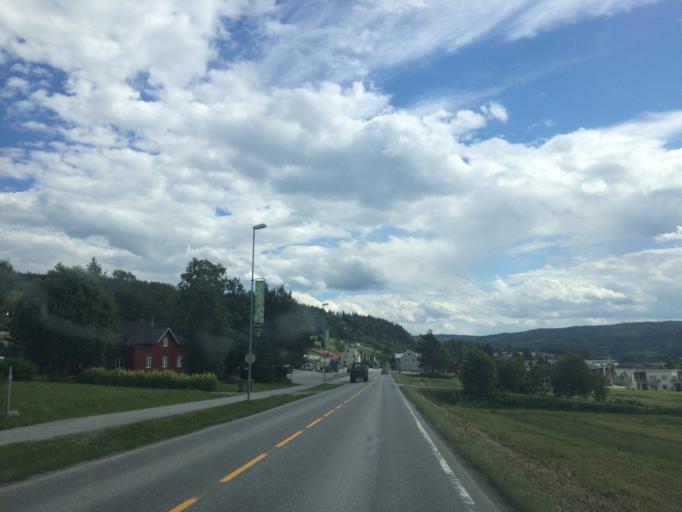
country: NO
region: Sor-Trondelag
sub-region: Selbu
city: Mebonden
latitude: 63.2228
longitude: 11.0351
